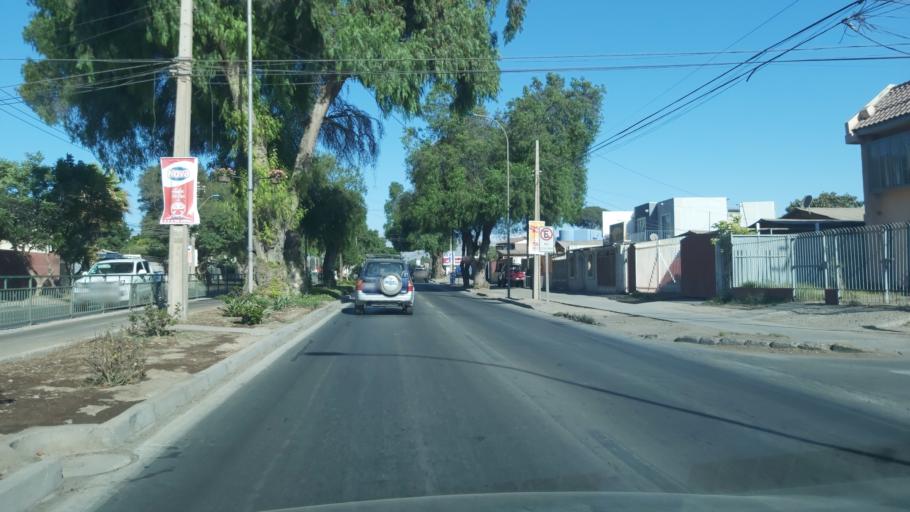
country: CL
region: Atacama
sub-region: Provincia de Copiapo
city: Copiapo
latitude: -27.3746
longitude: -70.3267
